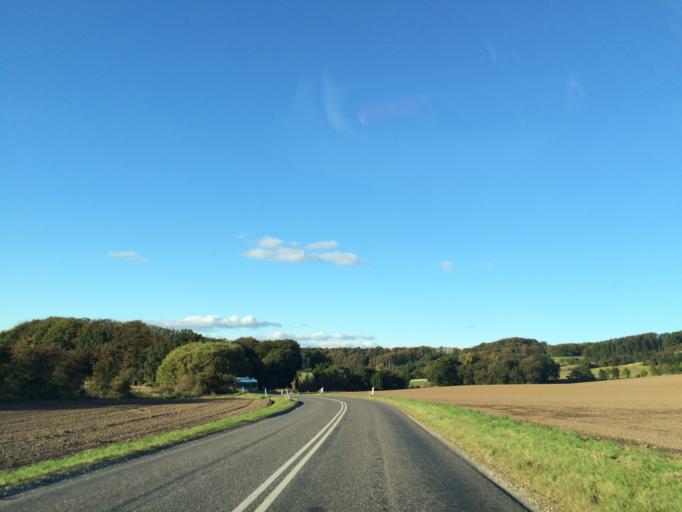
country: DK
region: Central Jutland
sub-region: Skanderborg Kommune
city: Ry
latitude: 56.1162
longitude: 9.7341
